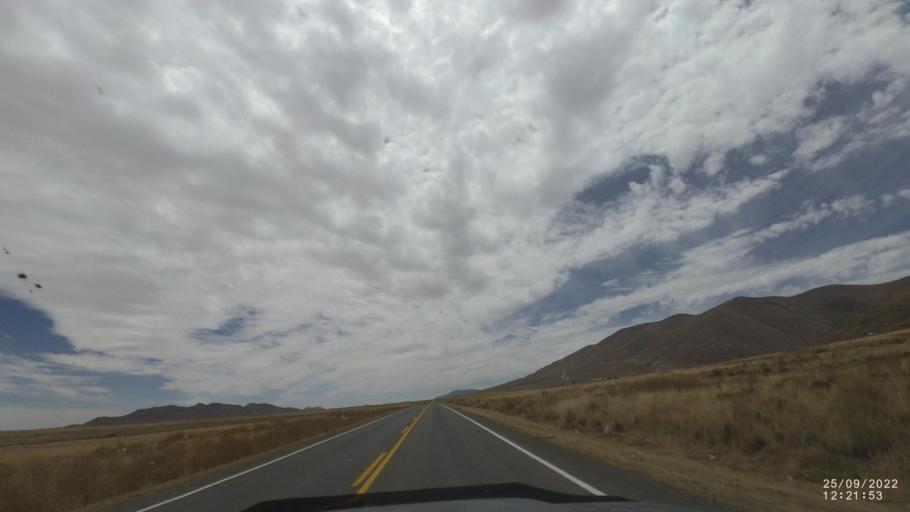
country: BO
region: Oruro
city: Poopo
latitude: -18.4032
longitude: -66.9771
